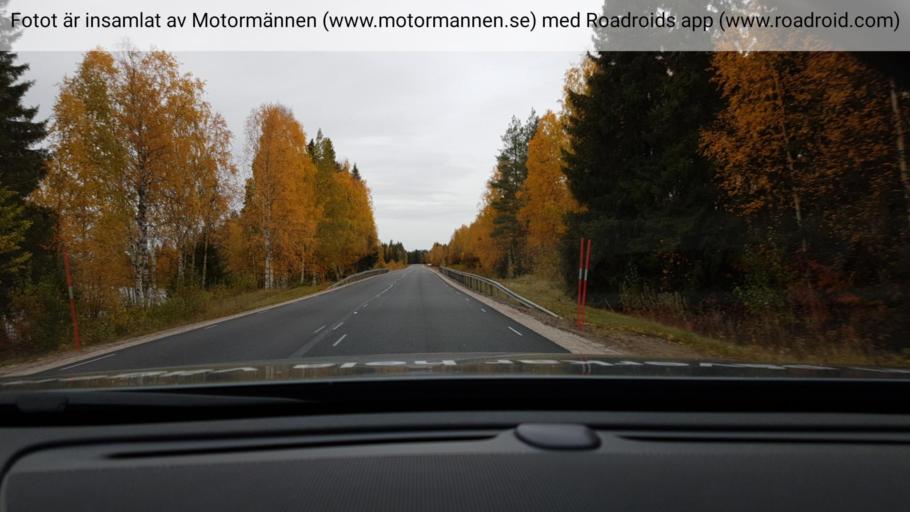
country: SE
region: Norrbotten
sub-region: Overkalix Kommun
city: OEverkalix
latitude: 66.4113
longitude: 22.8055
